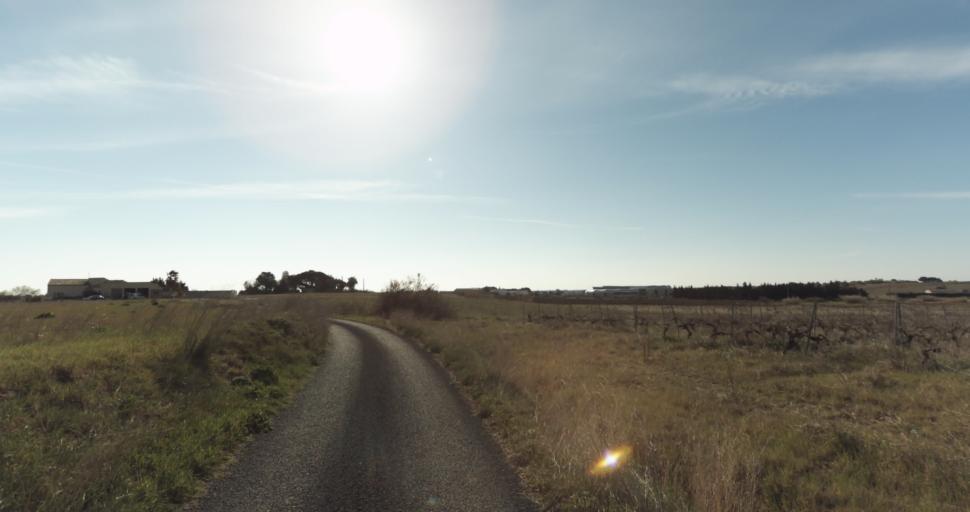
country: FR
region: Languedoc-Roussillon
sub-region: Departement de l'Herault
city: Marseillan
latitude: 43.3603
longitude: 3.5128
